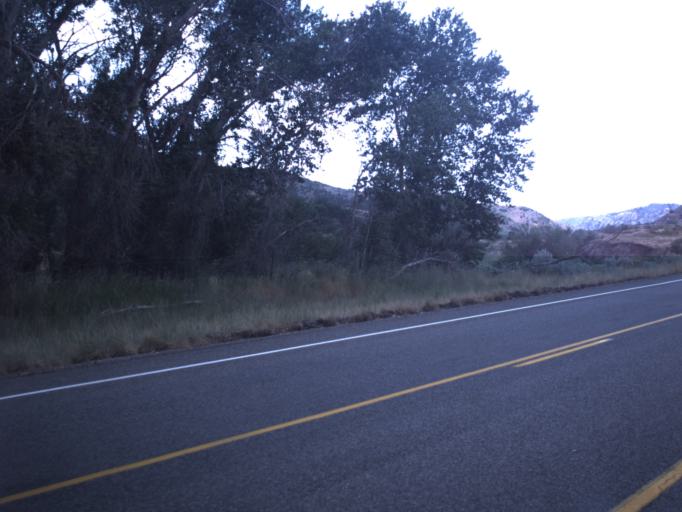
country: US
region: Utah
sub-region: Juab County
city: Nephi
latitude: 39.7183
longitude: -111.7302
